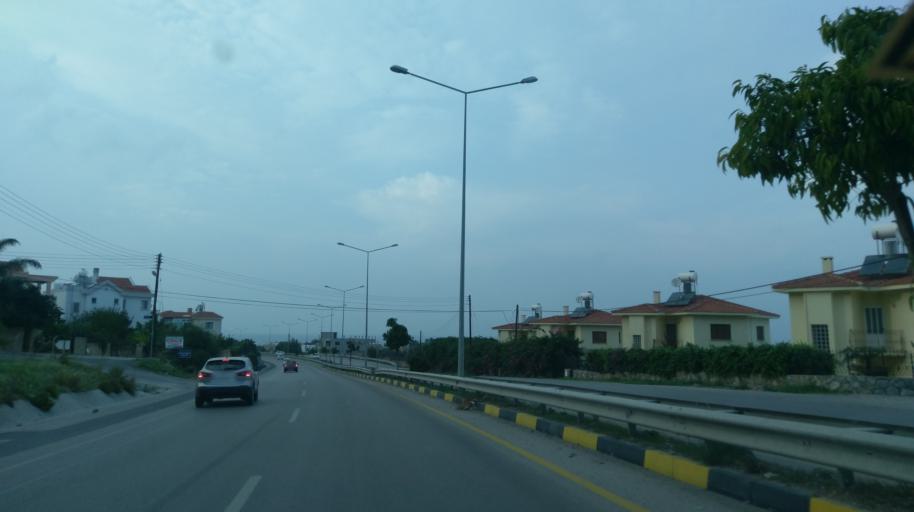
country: CY
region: Keryneia
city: Kyrenia
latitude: 35.3381
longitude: 33.2558
